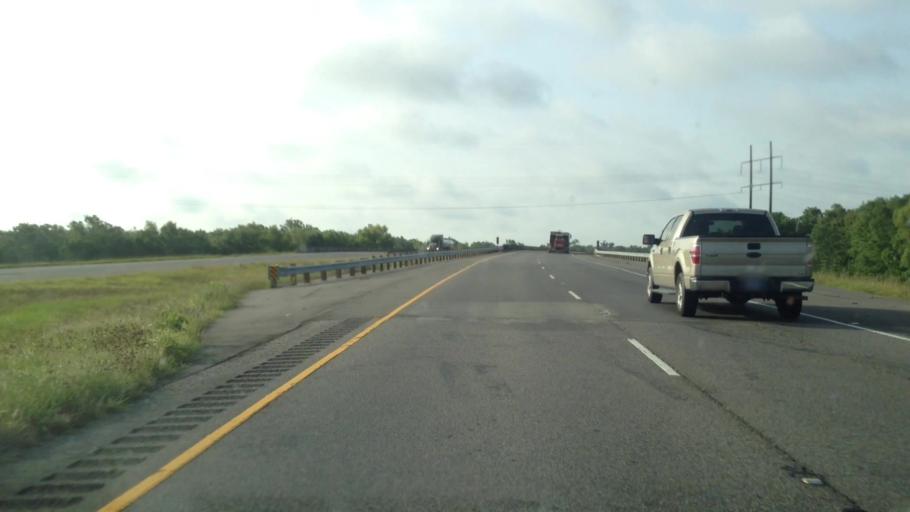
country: US
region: Louisiana
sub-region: Avoyelles Parish
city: Bunkie
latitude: 30.9006
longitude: -92.2301
